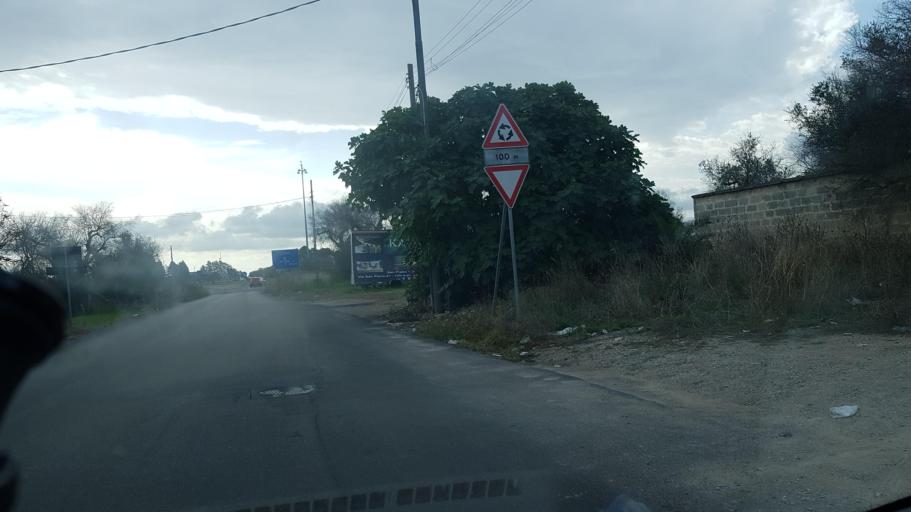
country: IT
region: Apulia
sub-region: Provincia di Brindisi
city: San Pietro Vernotico
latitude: 40.4780
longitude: 18.0070
